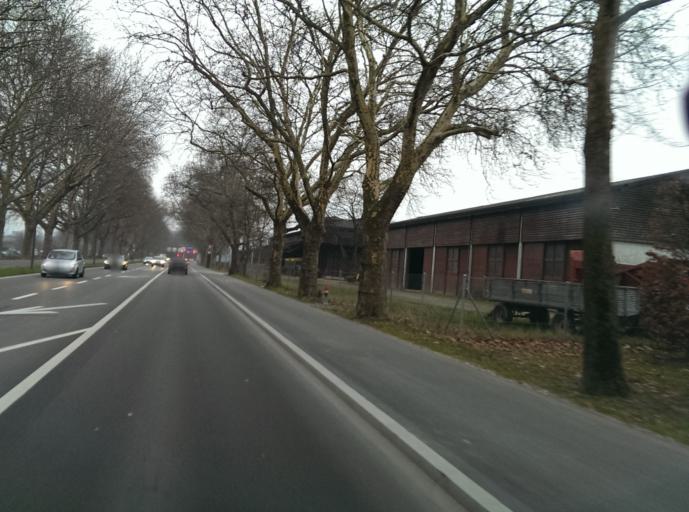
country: CH
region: Zurich
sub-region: Bezirk Dietikon
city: Oberengstringen
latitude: 47.3993
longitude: 8.4694
